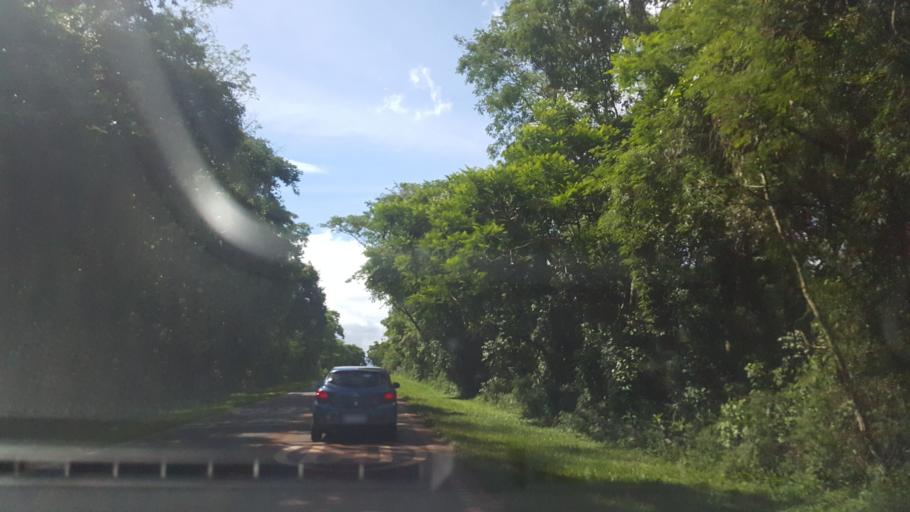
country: AR
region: Misiones
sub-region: Departamento de Iguazu
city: Puerto Iguazu
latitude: -25.6894
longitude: -54.4792
